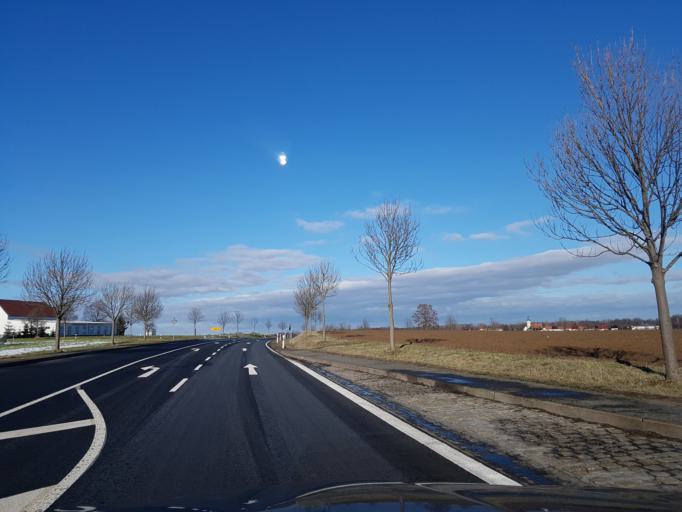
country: DE
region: Saxony
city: Priestewitz
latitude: 51.2398
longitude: 13.5510
